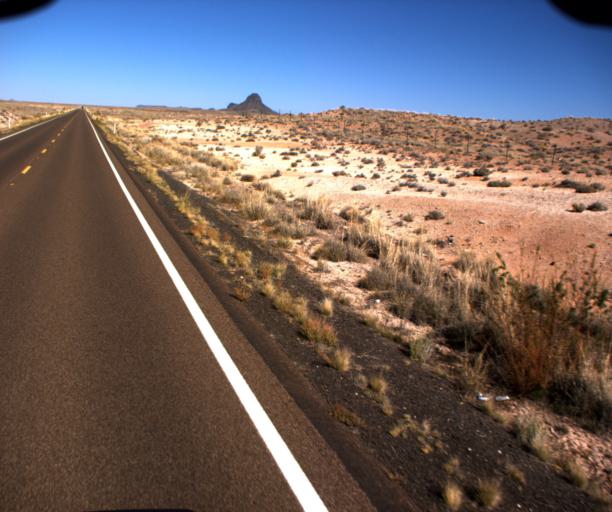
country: US
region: Arizona
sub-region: Navajo County
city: Dilkon
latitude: 35.2451
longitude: -110.4302
